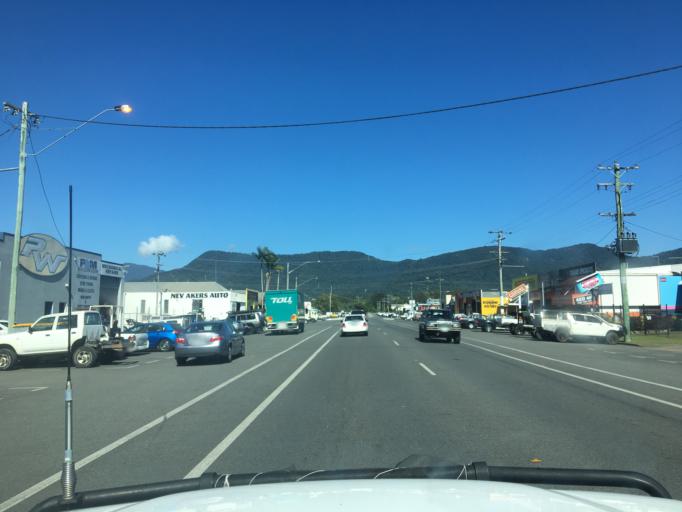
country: AU
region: Queensland
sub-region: Cairns
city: Woree
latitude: -16.9390
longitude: 145.7538
